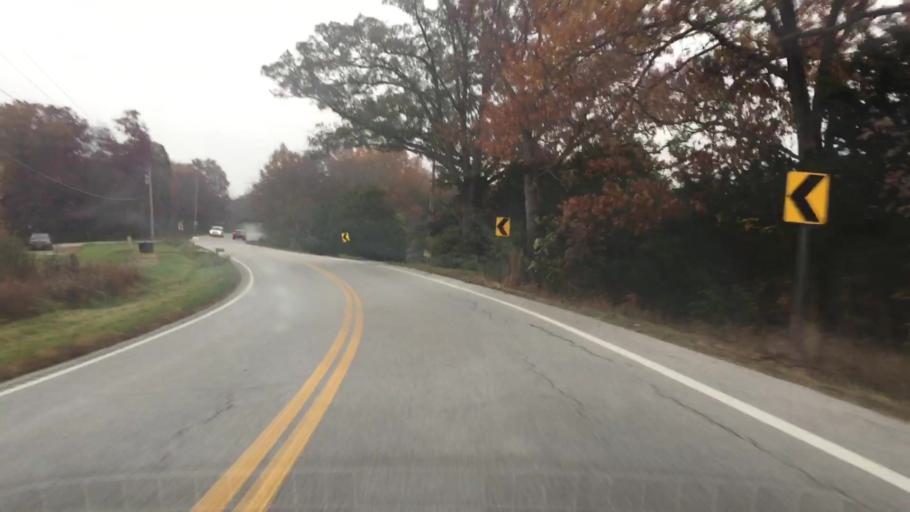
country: US
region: Missouri
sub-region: Callaway County
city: Fulton
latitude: 38.8780
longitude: -92.0833
